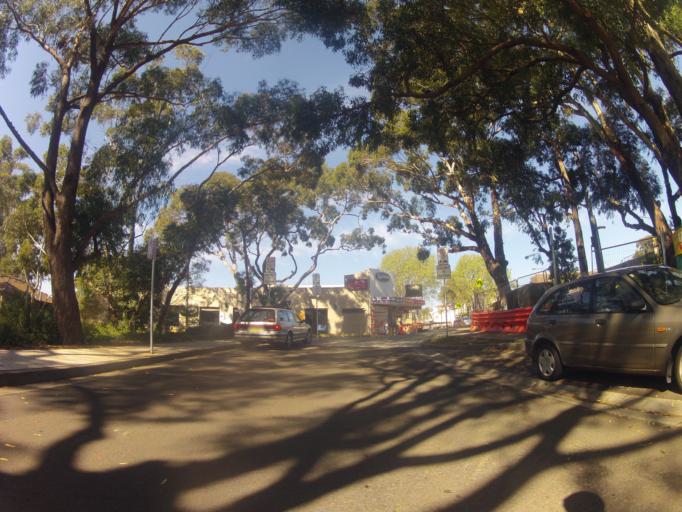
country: AU
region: New South Wales
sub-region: Sutherland Shire
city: Gymea
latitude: -34.0353
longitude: 151.0852
